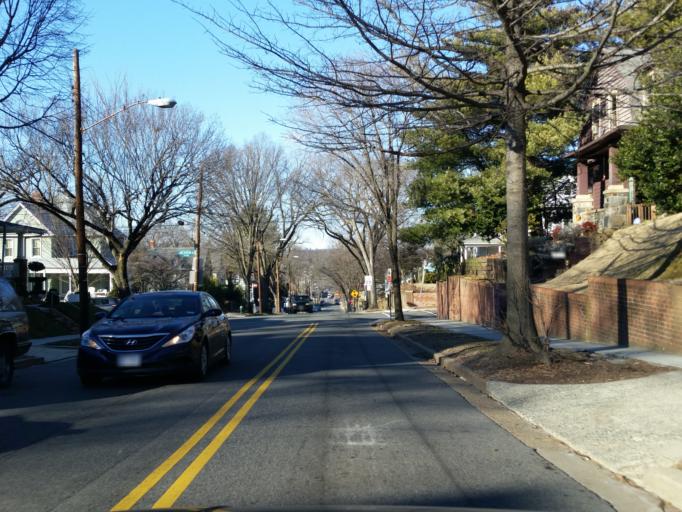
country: US
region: Maryland
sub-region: Prince George's County
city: Mount Rainier
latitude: 38.9297
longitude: -76.9793
